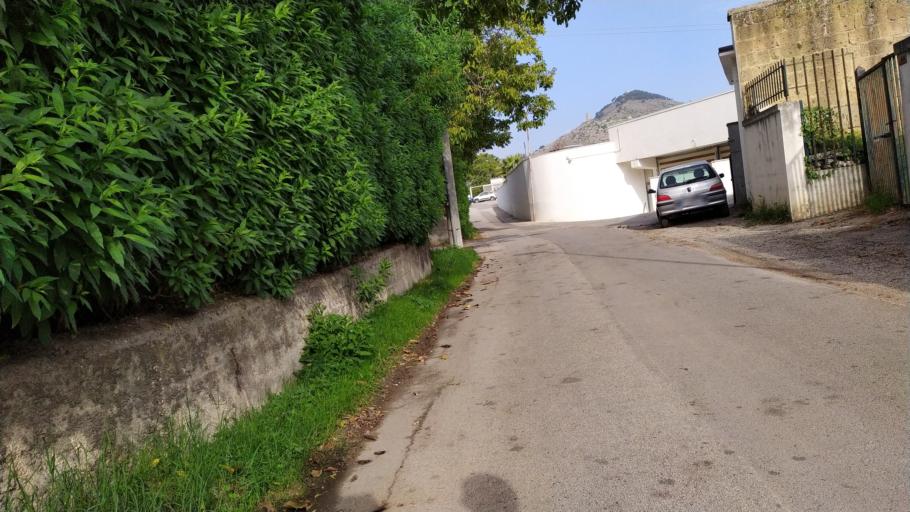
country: IT
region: Campania
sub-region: Provincia di Caserta
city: Maddaloni
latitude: 41.0287
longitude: 14.3964
